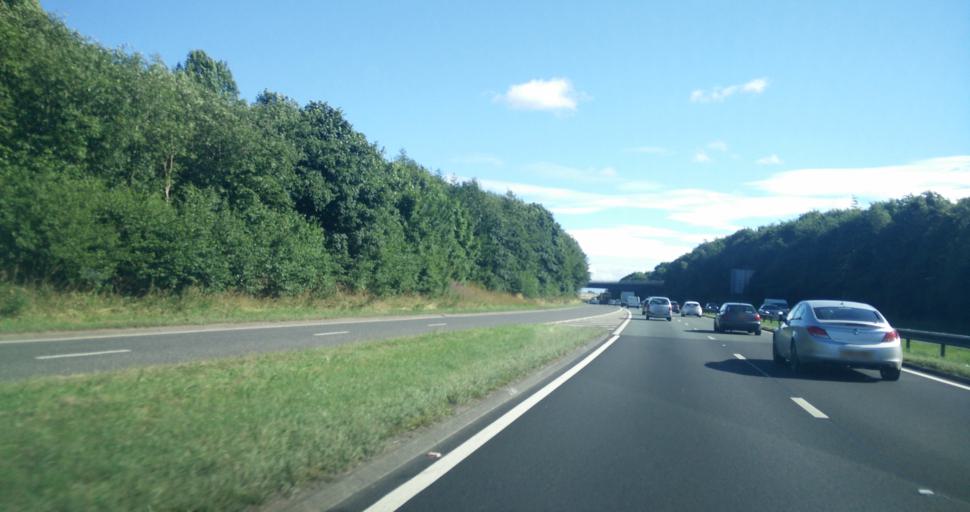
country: GB
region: England
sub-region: County Durham
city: Houghton-le-Spring
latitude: 54.8874
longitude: -1.4578
